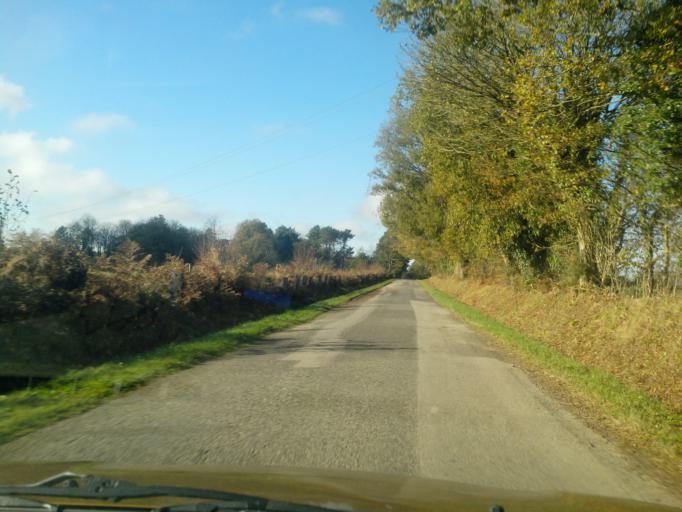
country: FR
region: Brittany
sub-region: Departement du Morbihan
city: Pleucadeuc
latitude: 47.7270
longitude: -2.3870
